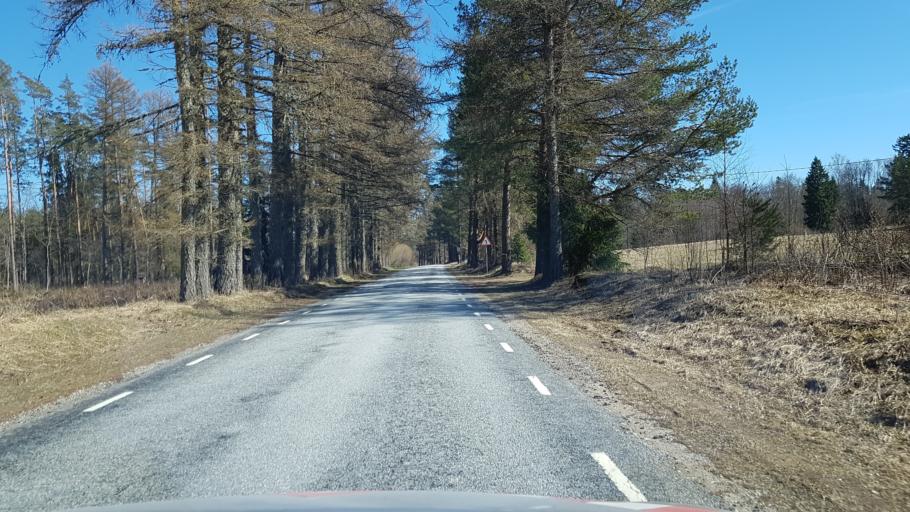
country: EE
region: Laeaene-Virumaa
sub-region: Someru vald
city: Someru
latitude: 59.3317
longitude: 26.5545
